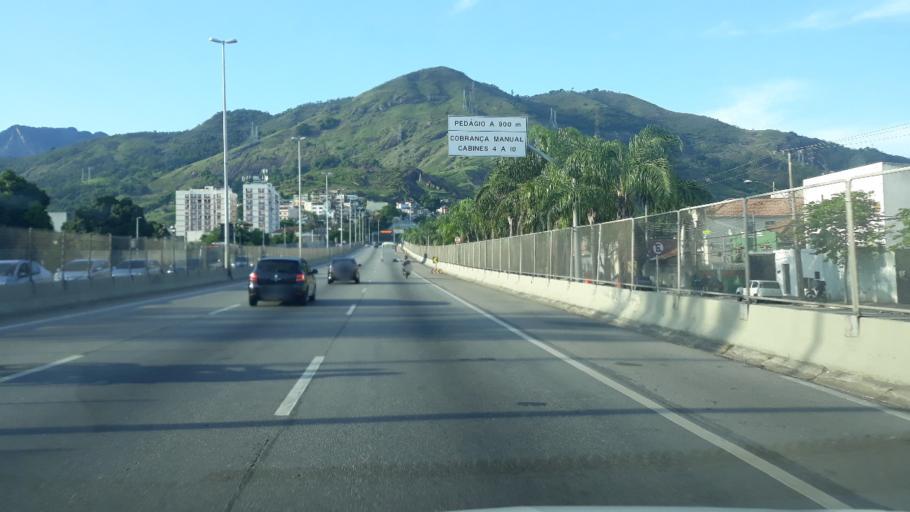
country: BR
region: Rio de Janeiro
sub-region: Rio De Janeiro
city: Rio de Janeiro
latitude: -22.9015
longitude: -43.3037
